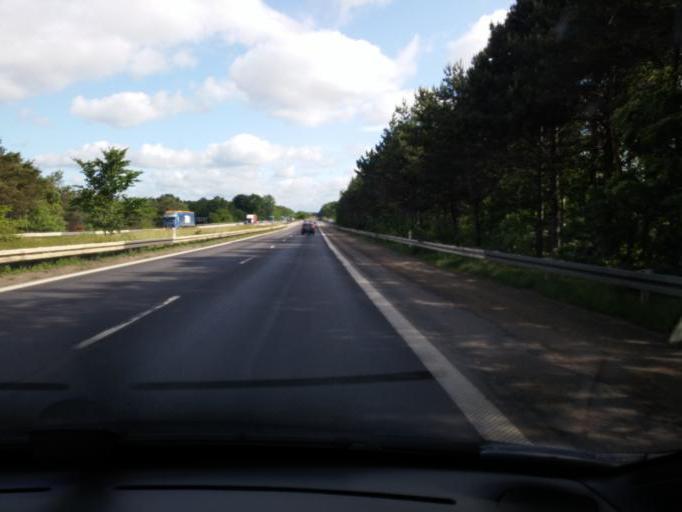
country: DK
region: Capital Region
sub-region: Fureso Kommune
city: Farum
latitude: 55.8025
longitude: 12.3797
